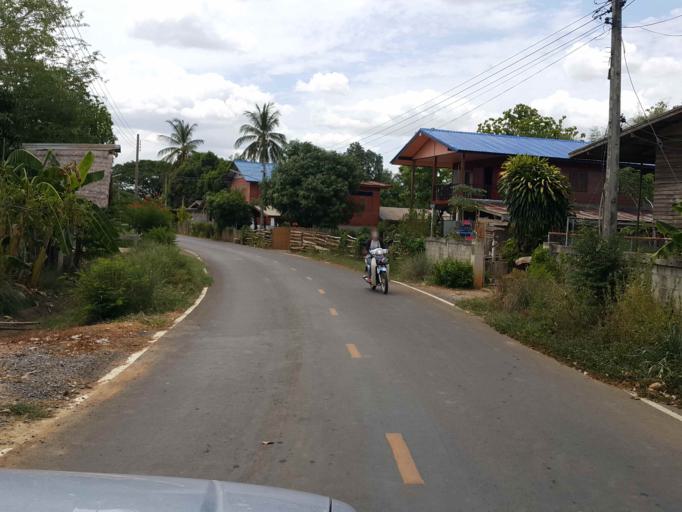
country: TH
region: Sukhothai
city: Thung Saliam
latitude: 17.3267
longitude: 99.5590
